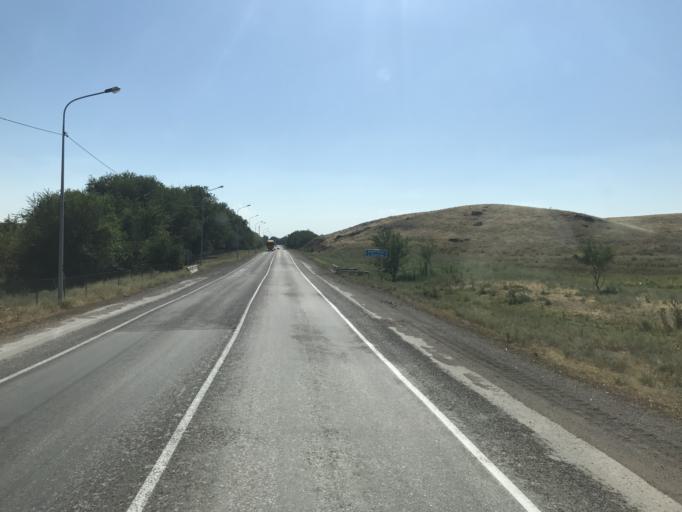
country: KZ
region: Zhambyl
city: Georgiyevka
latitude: 43.2406
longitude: 74.7747
